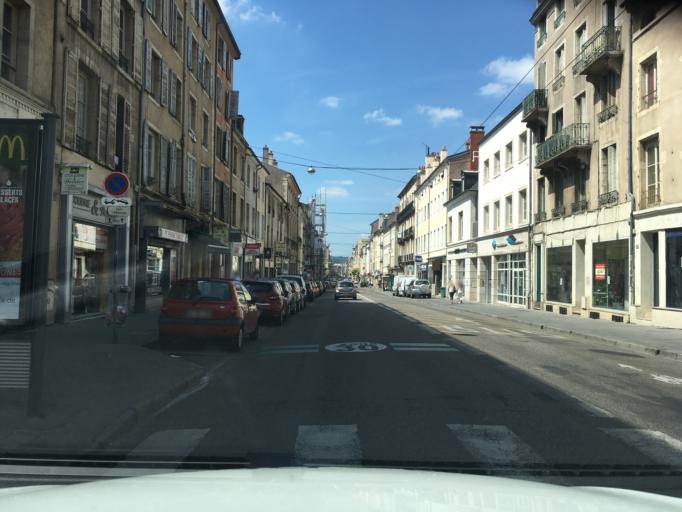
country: FR
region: Lorraine
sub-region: Departement de Meurthe-et-Moselle
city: Nancy
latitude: 48.6869
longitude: 6.1853
